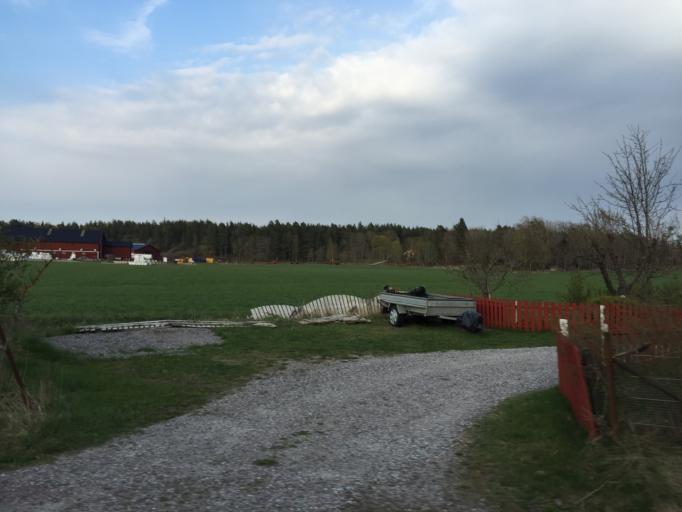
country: SE
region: Soedermanland
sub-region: Trosa Kommun
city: Vagnharad
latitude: 59.0068
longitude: 17.5966
